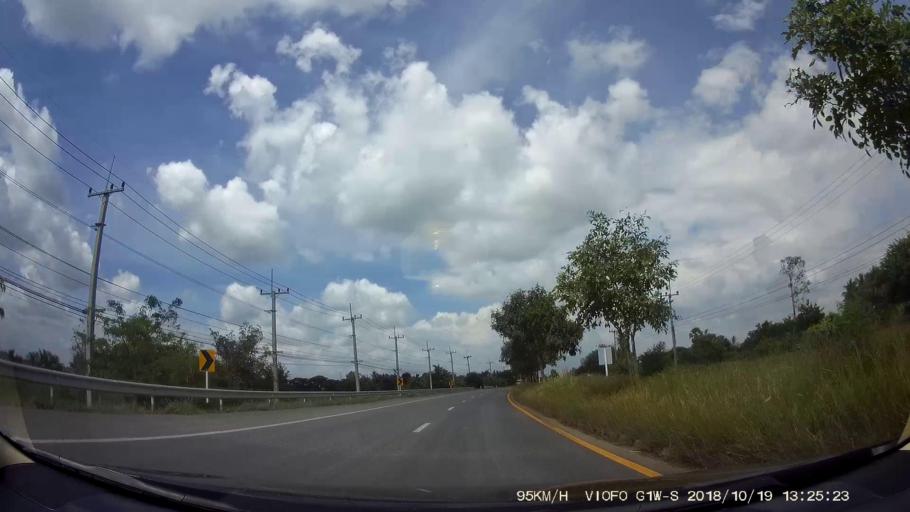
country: TH
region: Chaiyaphum
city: Chatturat
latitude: 15.5205
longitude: 101.8256
